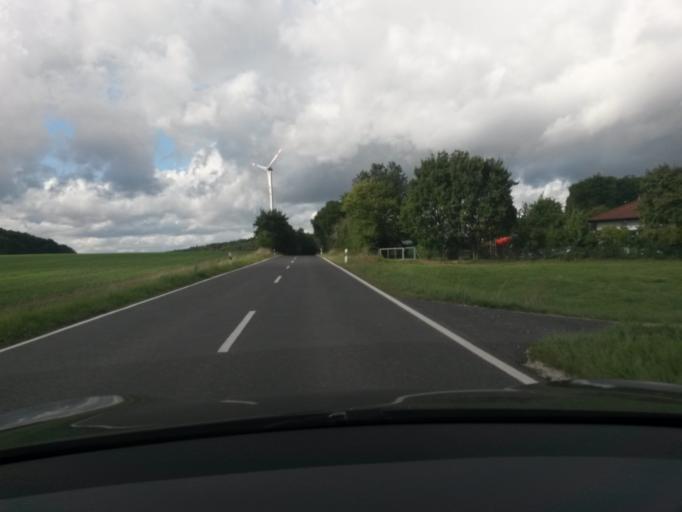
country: DE
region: Bavaria
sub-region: Upper Palatinate
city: Hohenfels
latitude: 49.1450
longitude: 11.8498
